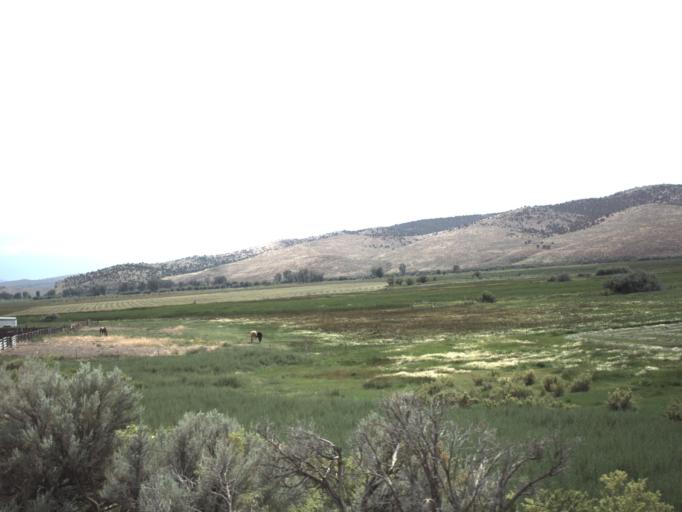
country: US
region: Utah
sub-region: Piute County
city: Junction
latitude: 38.1151
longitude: -111.9942
